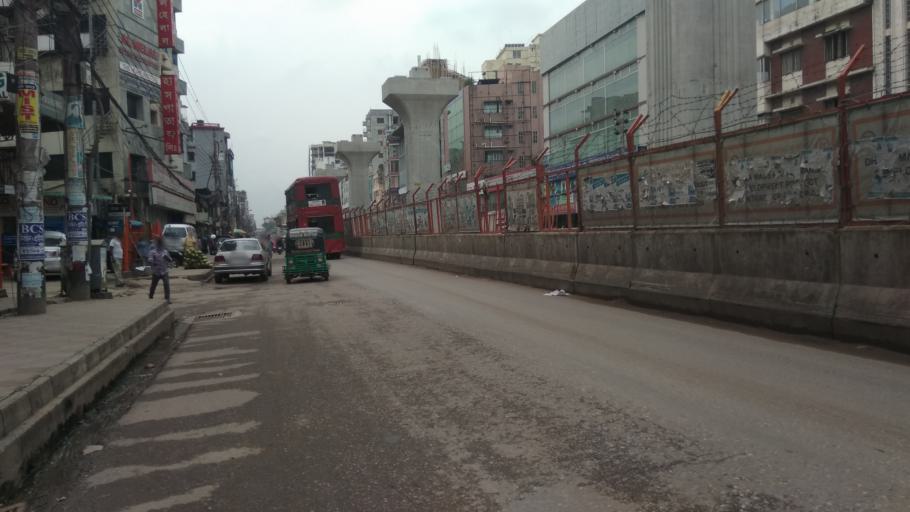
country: BD
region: Dhaka
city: Azimpur
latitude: 23.8031
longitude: 90.3705
